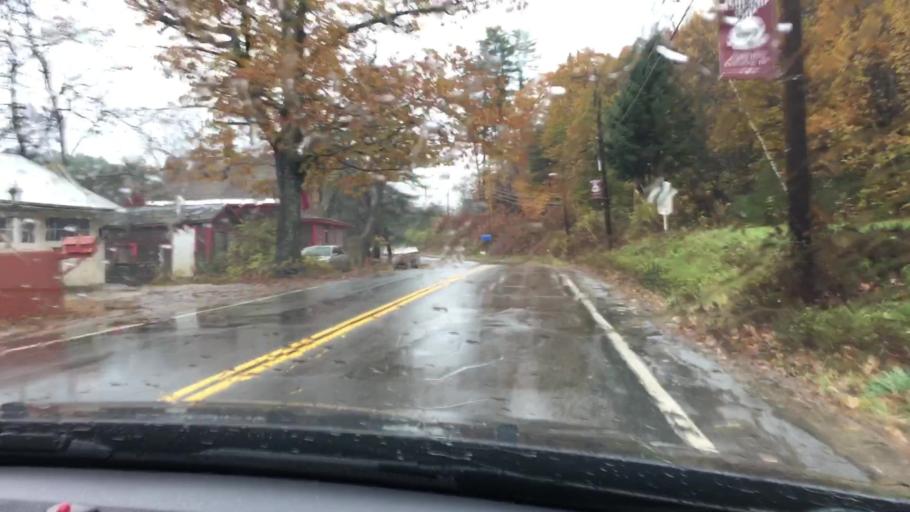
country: US
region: New Hampshire
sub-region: Grafton County
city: Ashland
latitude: 43.7018
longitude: -71.6305
